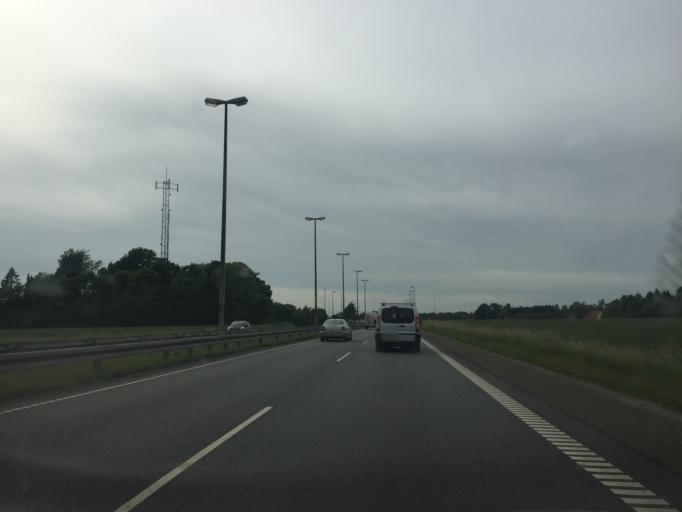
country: DK
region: Capital Region
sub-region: Hoje-Taastrup Kommune
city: Taastrup
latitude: 55.6328
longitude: 12.2911
